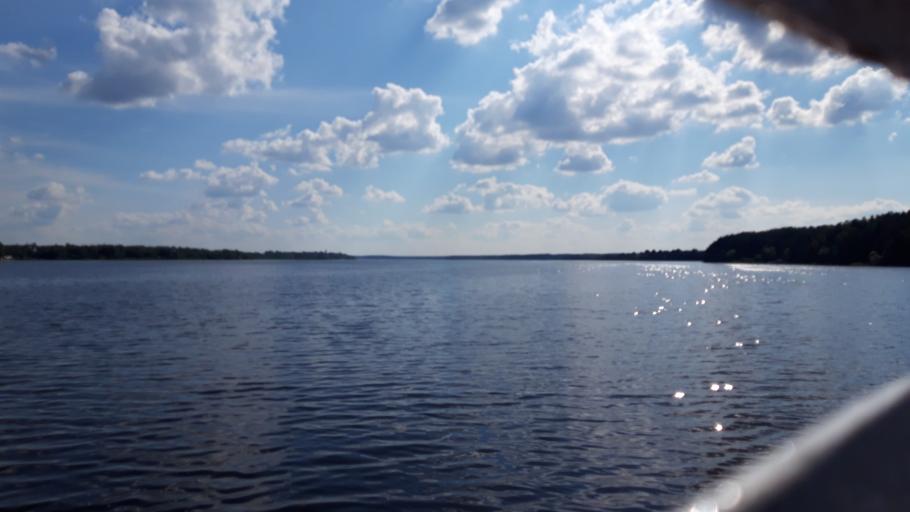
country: RU
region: Tverskaya
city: Konakovo
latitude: 56.6578
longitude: 36.6394
